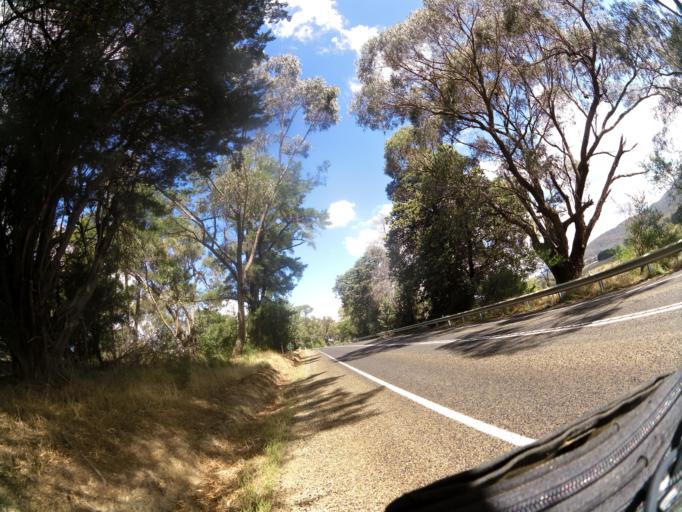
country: AU
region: Victoria
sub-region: Mansfield
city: Mansfield
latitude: -36.8283
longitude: 146.0084
